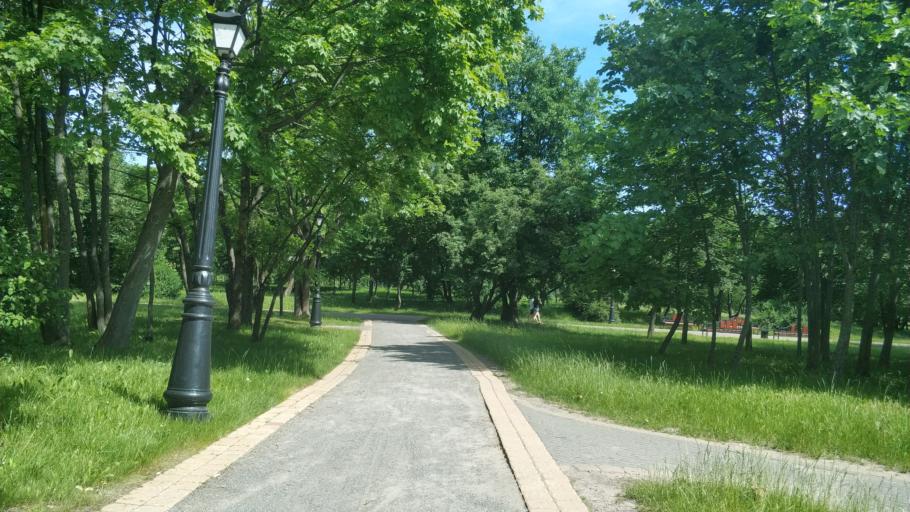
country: BY
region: Minsk
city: Minsk
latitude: 53.8542
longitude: 27.5845
